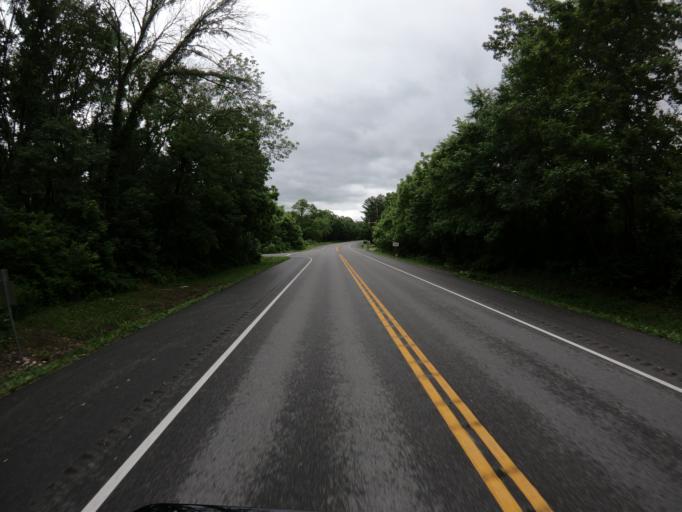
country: US
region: Maryland
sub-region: Washington County
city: Keedysville
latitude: 39.4957
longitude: -77.6864
